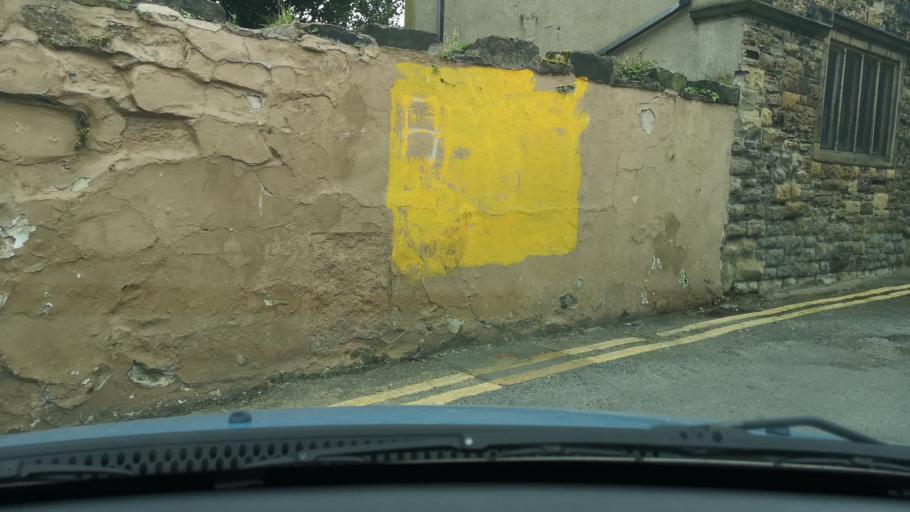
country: GB
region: England
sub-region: City and Borough of Wakefield
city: Pontefract
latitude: 53.6948
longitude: -1.3041
